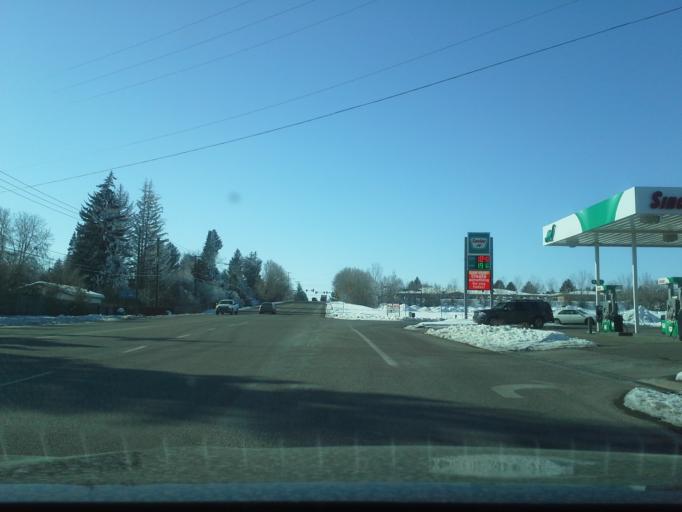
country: US
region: Idaho
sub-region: Bonneville County
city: Idaho Falls
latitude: 43.5041
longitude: -112.0590
